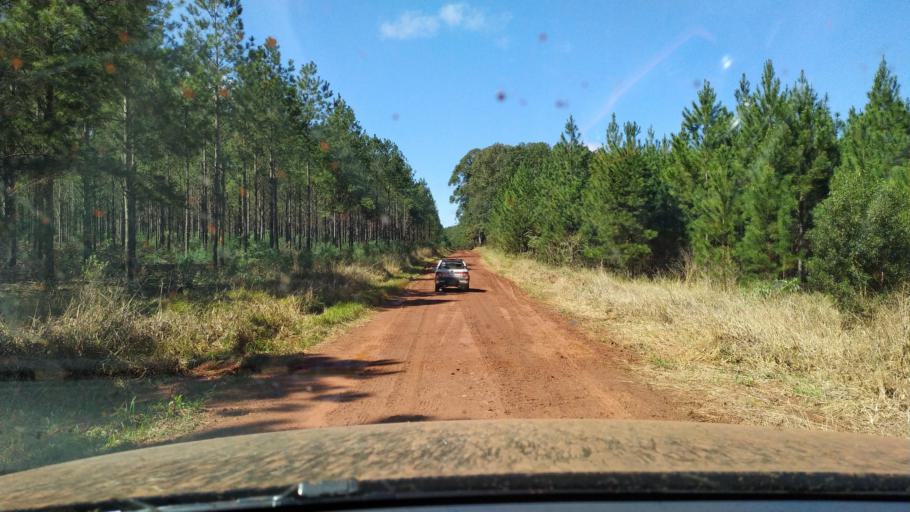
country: AR
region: Corrientes
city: Santo Tome
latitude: -28.3971
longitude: -56.0196
